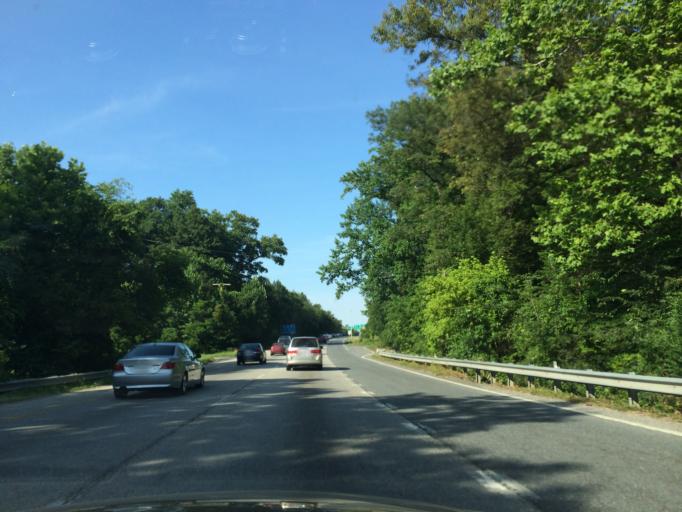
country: US
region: Maryland
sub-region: Anne Arundel County
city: Gambrills
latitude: 39.0585
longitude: -76.6535
